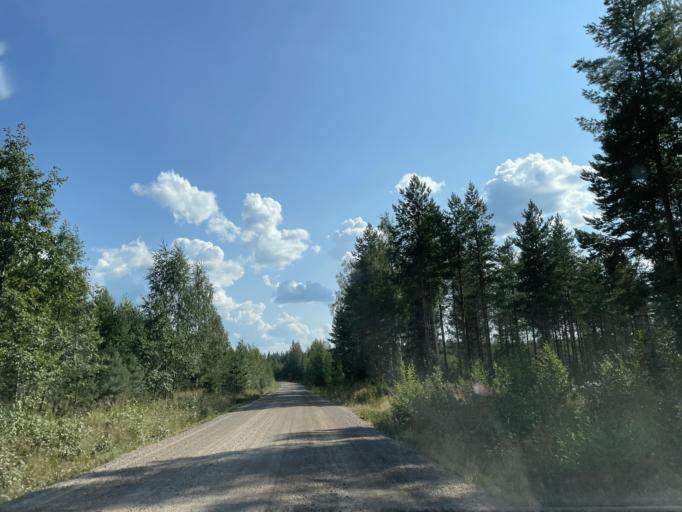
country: FI
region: Central Finland
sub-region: Saarijaervi-Viitasaari
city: Pihtipudas
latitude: 63.3496
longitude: 25.7900
